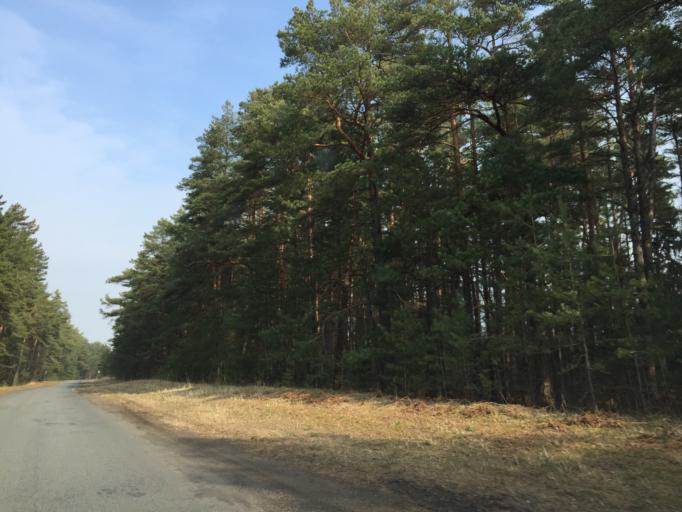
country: LV
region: Salacgrivas
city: Ainazi
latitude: 57.8880
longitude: 24.3681
